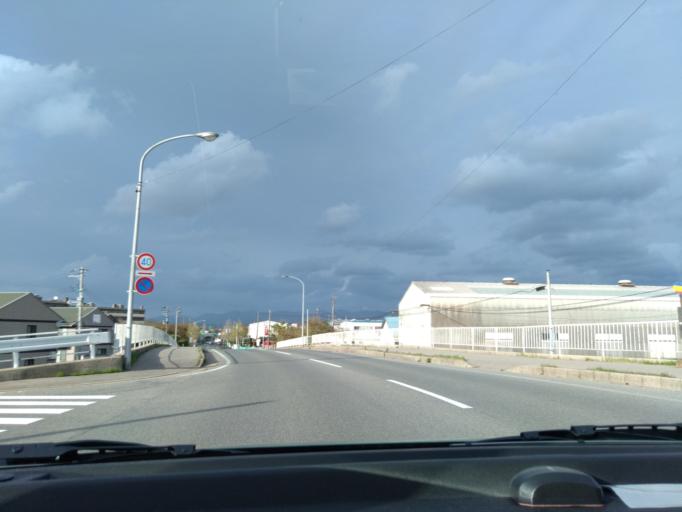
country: JP
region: Akita
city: Akita Shi
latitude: 39.7559
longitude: 140.0757
